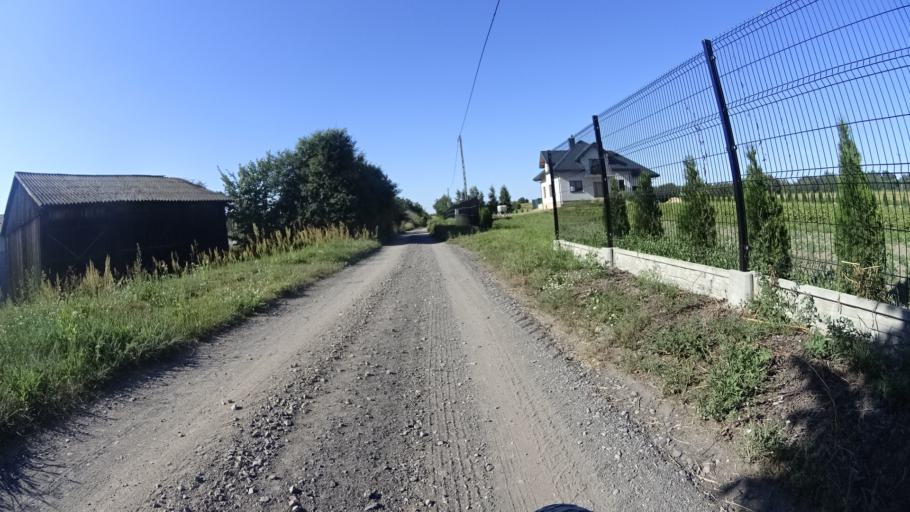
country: PL
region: Masovian Voivodeship
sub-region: Powiat bialobrzeski
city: Wysmierzyce
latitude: 51.6655
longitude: 20.8496
